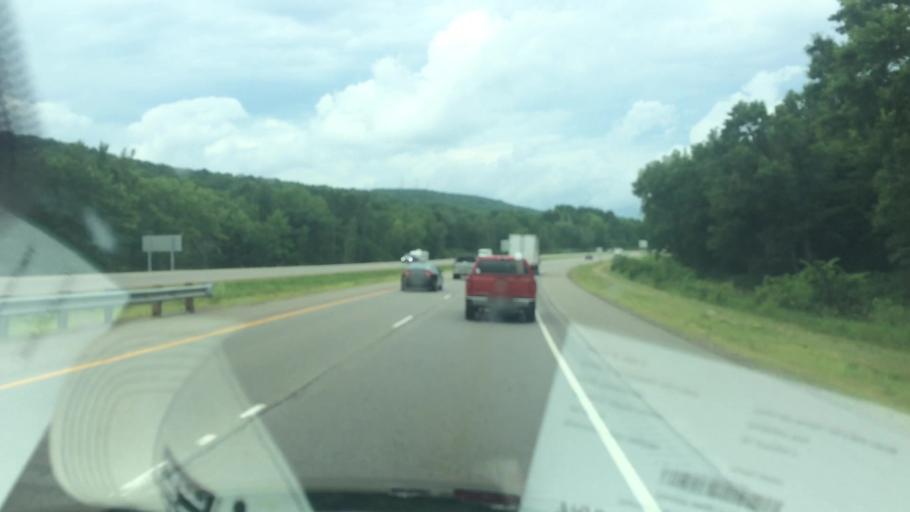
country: US
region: Wisconsin
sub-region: Marathon County
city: Evergreen
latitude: 44.8697
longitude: -89.6452
